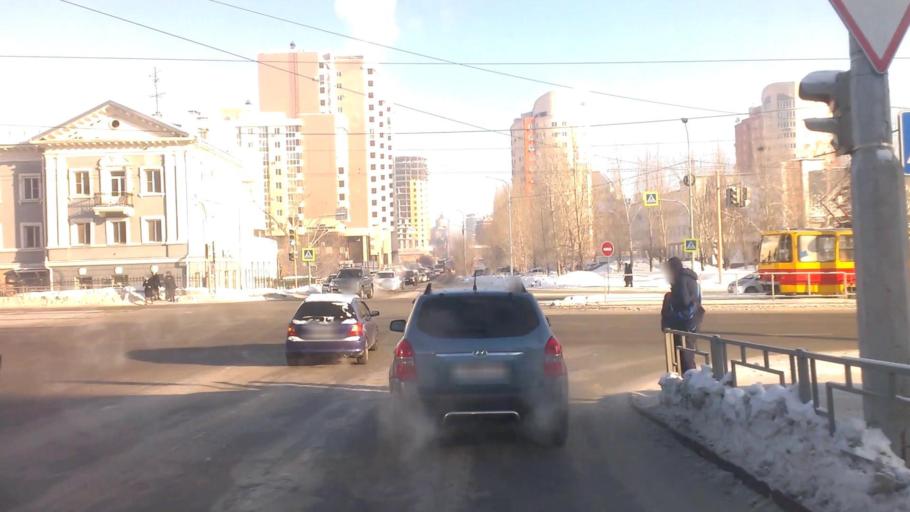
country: RU
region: Altai Krai
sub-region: Gorod Barnaulskiy
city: Barnaul
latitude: 53.3360
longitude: 83.7758
